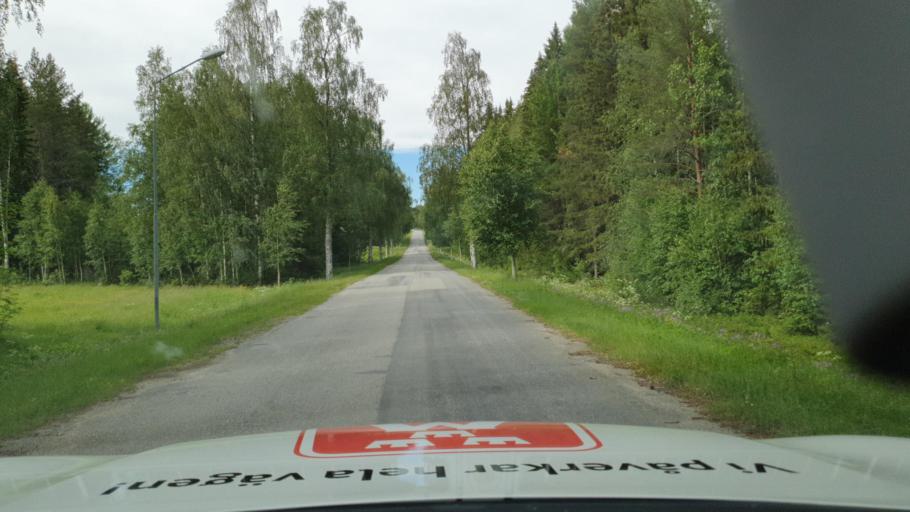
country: SE
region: Vaesterbotten
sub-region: Skelleftea Kommun
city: Burtraesk
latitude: 64.4309
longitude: 20.5193
